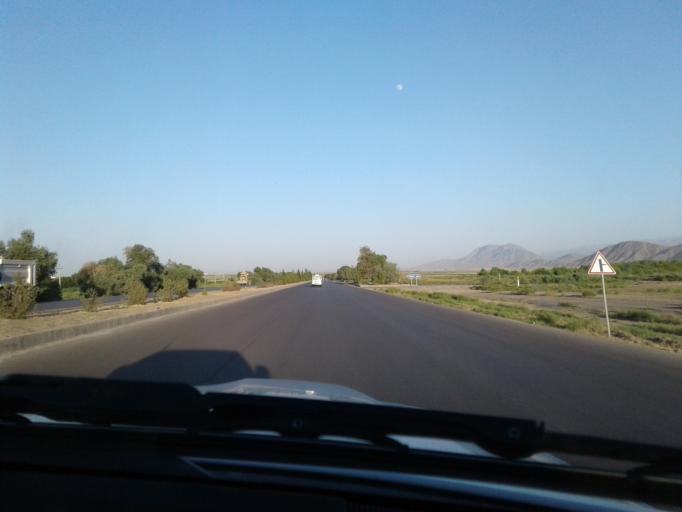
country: TM
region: Ahal
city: Arcabil
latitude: 38.1934
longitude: 57.8380
